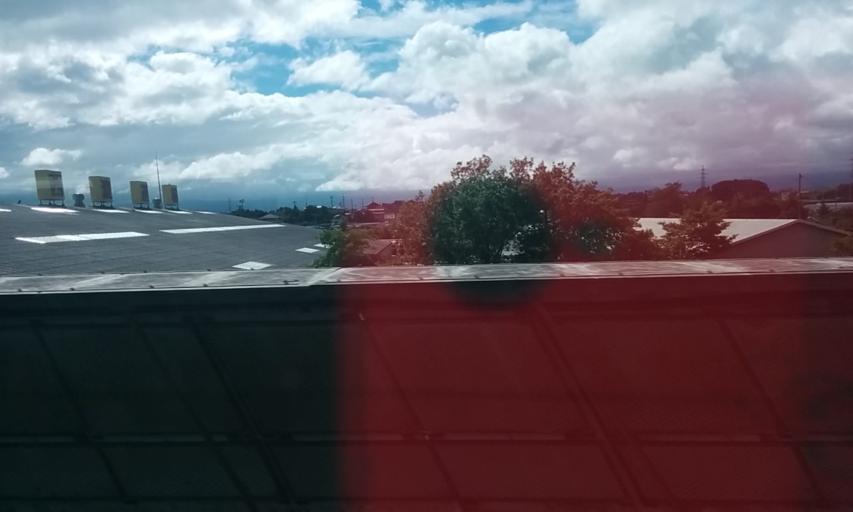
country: JP
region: Fukushima
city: Sukagawa
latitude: 37.3330
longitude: 140.3638
